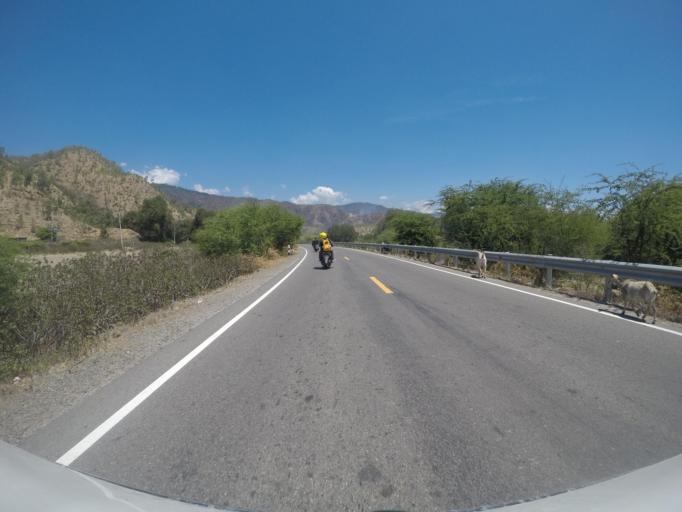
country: ID
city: Metinaro
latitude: -8.5274
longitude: 125.7098
